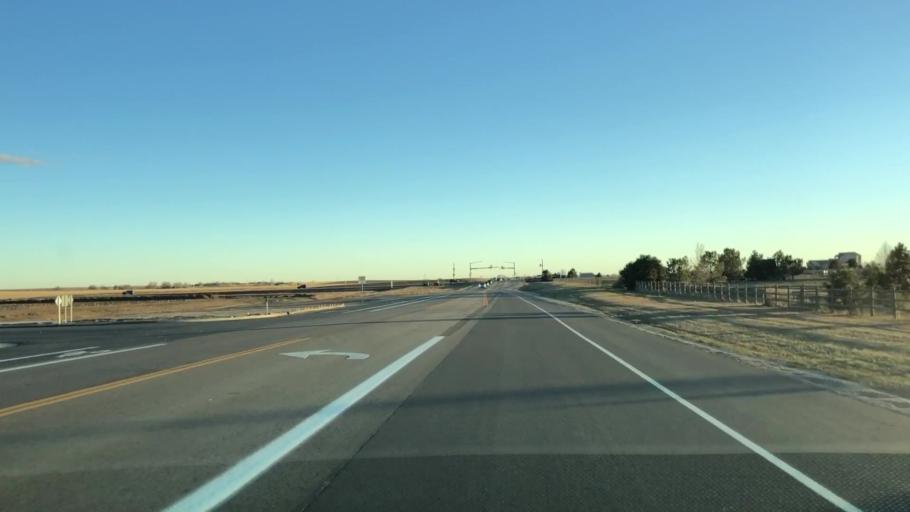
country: US
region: Colorado
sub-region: Weld County
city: Windsor
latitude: 40.4393
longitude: -104.9443
